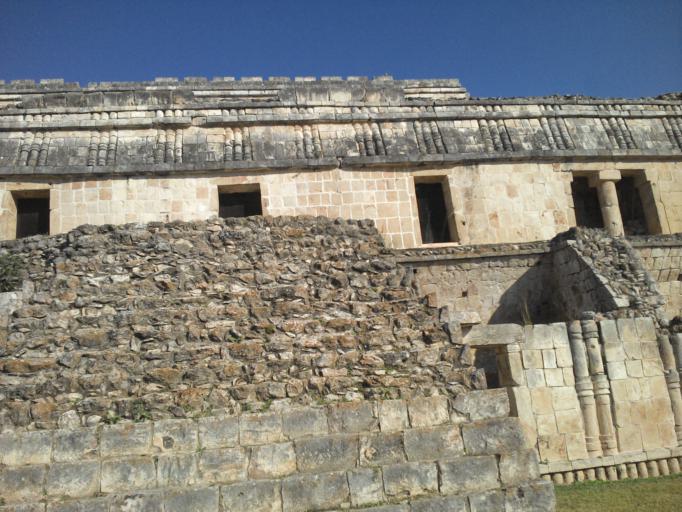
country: MX
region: Yucatan
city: Santa Elena
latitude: 20.2484
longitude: -89.6466
